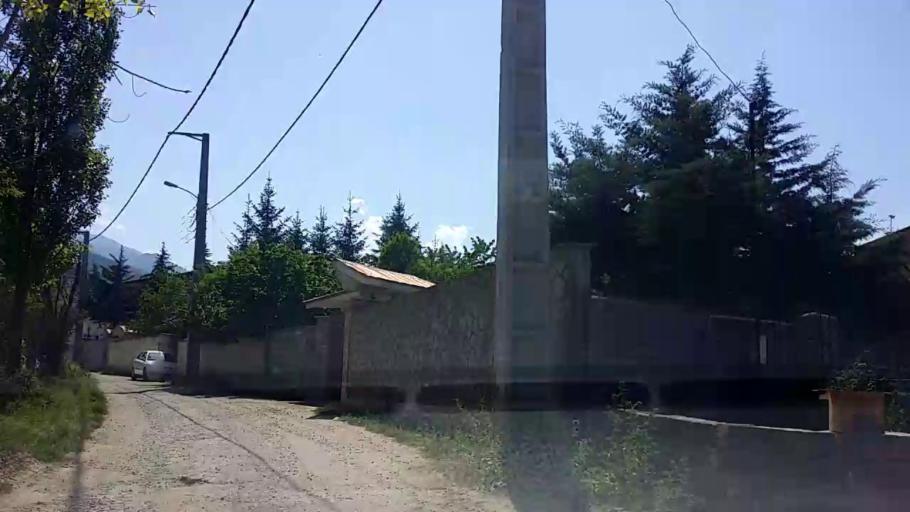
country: IR
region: Mazandaran
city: `Abbasabad
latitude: 36.5085
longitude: 51.1969
